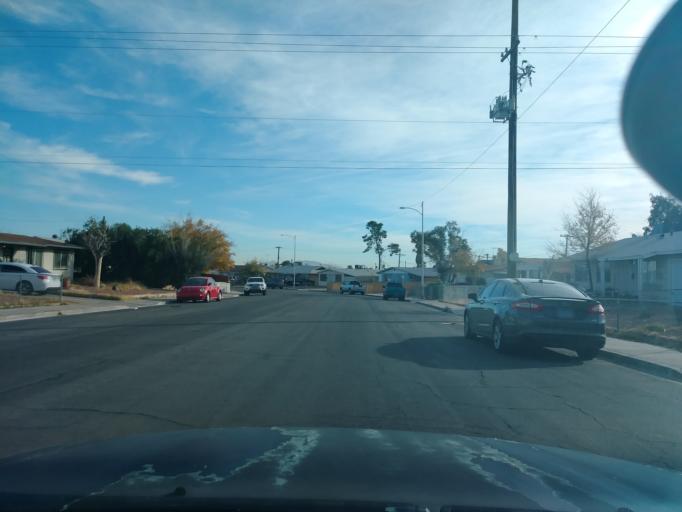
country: US
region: Nevada
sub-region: Clark County
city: Spring Valley
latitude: 36.1622
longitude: -115.2306
